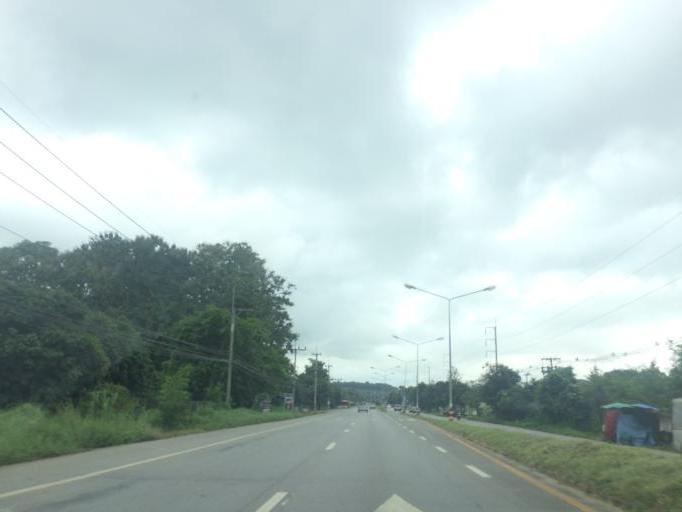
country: TH
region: Chiang Rai
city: Mae Chan
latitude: 20.1026
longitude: 99.8739
